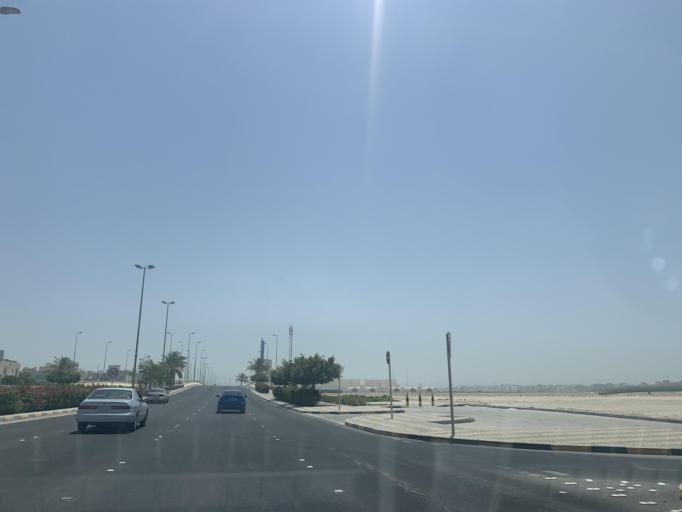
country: BH
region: Manama
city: Jidd Hafs
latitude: 26.2323
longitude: 50.4549
